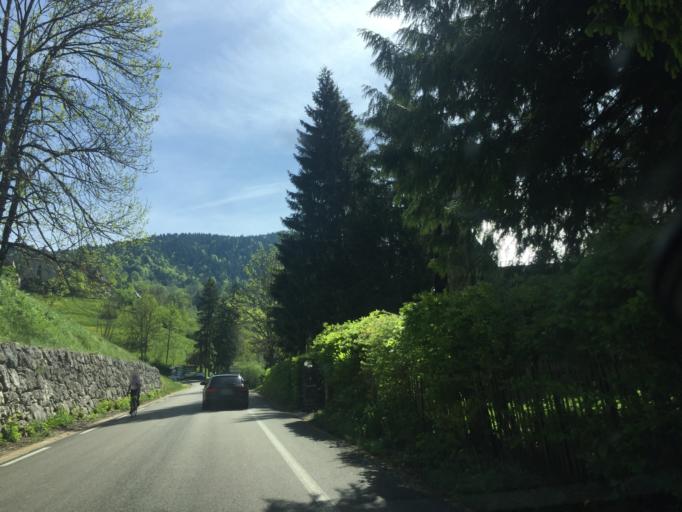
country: FR
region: Rhone-Alpes
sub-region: Departement de l'Isere
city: Saint-Hilaire
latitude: 45.3404
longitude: 5.8121
